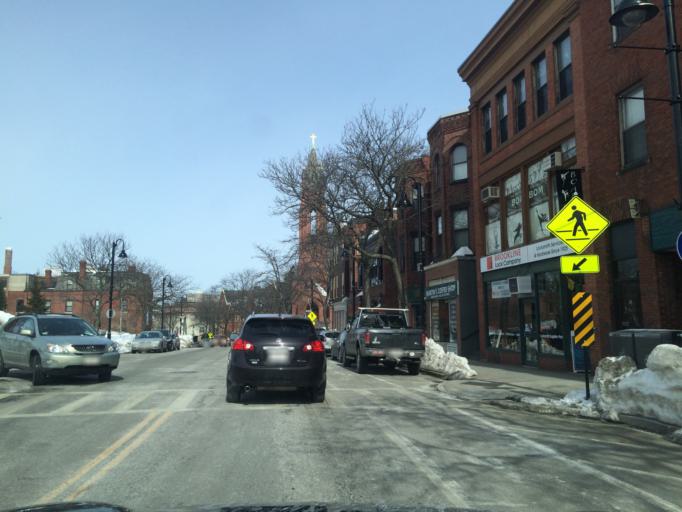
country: US
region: Massachusetts
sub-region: Norfolk County
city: Brookline
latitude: 42.3342
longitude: -71.1190
